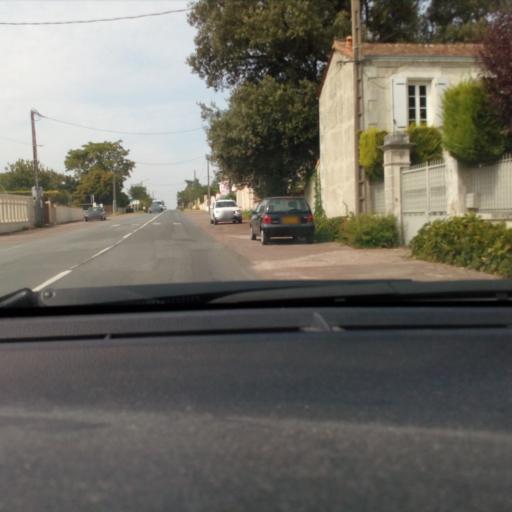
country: FR
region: Poitou-Charentes
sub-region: Departement de la Charente
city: Saint-Yrieix-sur-Charente
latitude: 45.6825
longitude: 0.1145
